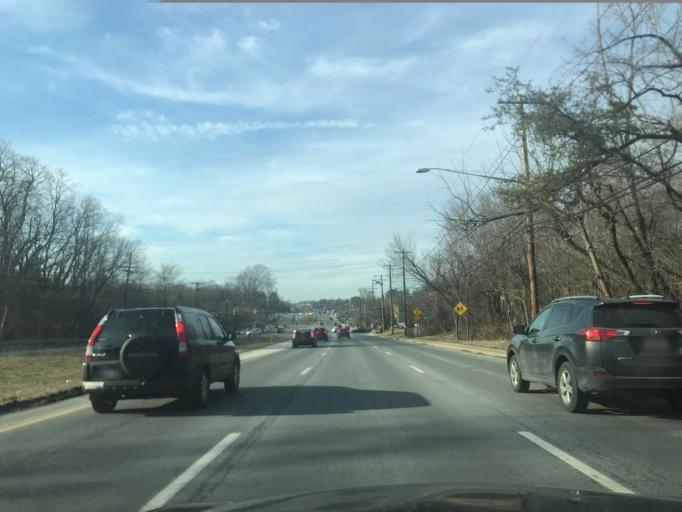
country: US
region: Maryland
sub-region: Montgomery County
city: Aspen Hill
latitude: 39.0765
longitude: -77.0693
